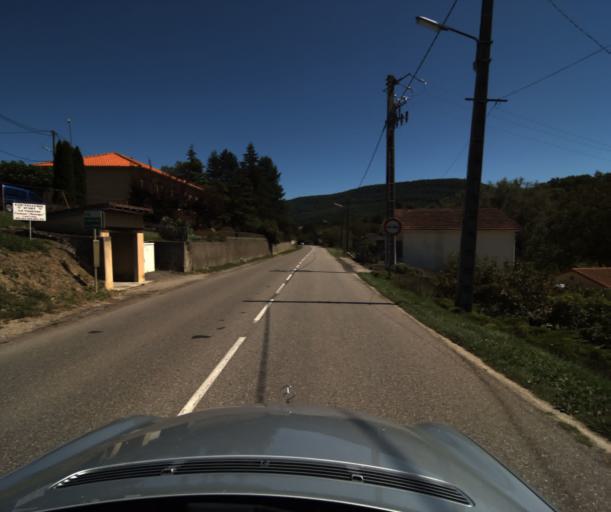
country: FR
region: Midi-Pyrenees
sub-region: Departement de l'Ariege
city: Lavelanet
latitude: 42.9572
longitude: 1.9009
